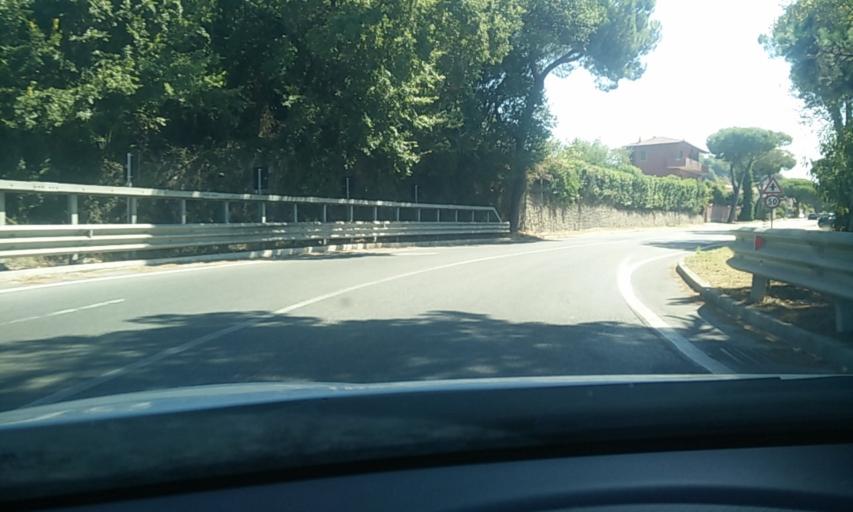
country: IT
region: Tuscany
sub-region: Provincia di Massa-Carrara
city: Carrara
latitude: 44.0433
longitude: 10.0869
